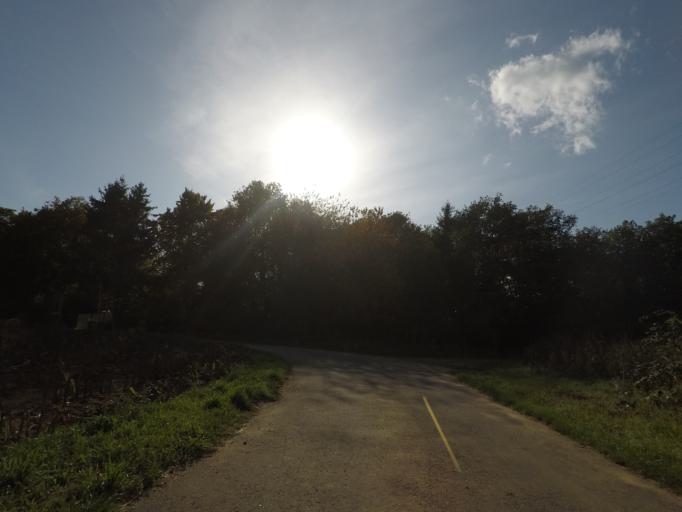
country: LU
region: Luxembourg
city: Itzig
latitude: 49.5965
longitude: 6.1733
